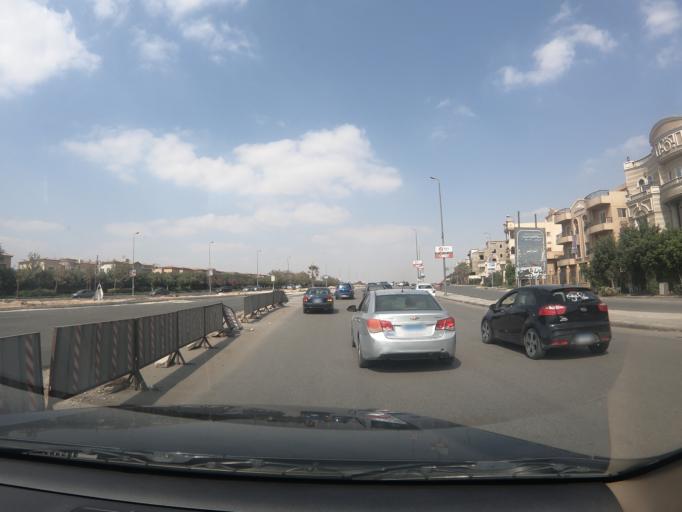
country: EG
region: Muhafazat al Qahirah
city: Cairo
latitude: 30.0162
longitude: 31.4461
